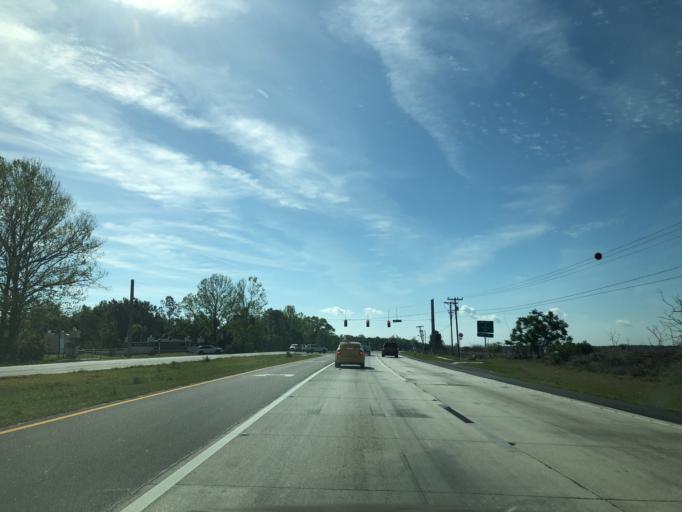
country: US
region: Florida
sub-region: Orange County
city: Zellwood
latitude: 28.7131
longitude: -81.5855
